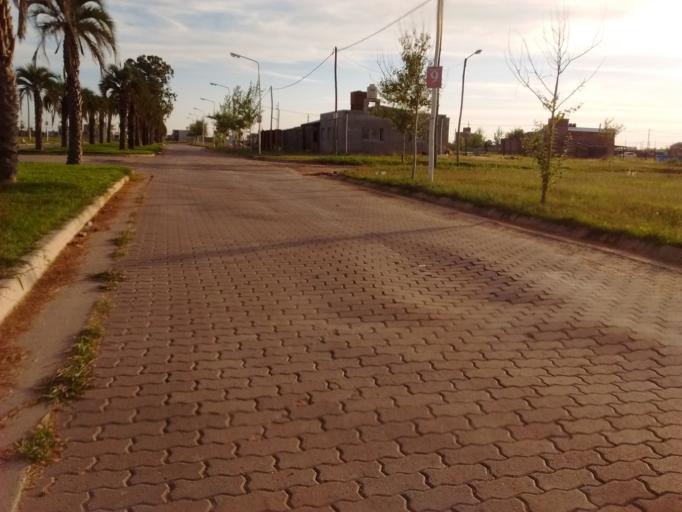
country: AR
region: Santa Fe
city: Roldan
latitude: -32.9335
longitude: -60.8762
